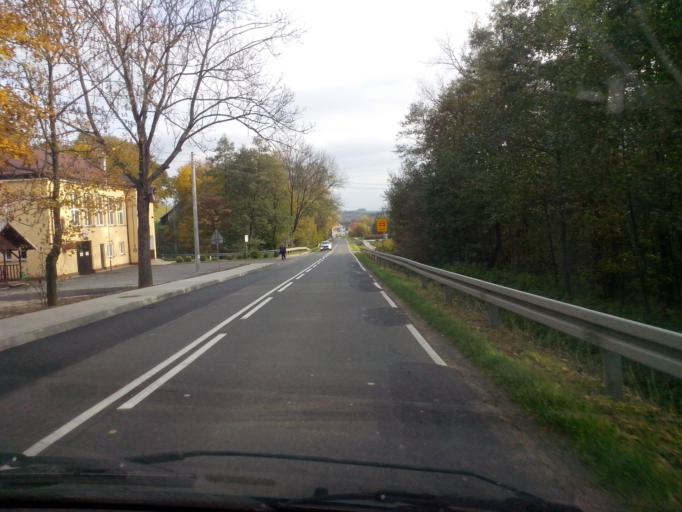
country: PL
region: Subcarpathian Voivodeship
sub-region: Powiat ropczycko-sedziszowski
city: Wielopole Skrzynskie
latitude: 49.9068
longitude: 21.6255
